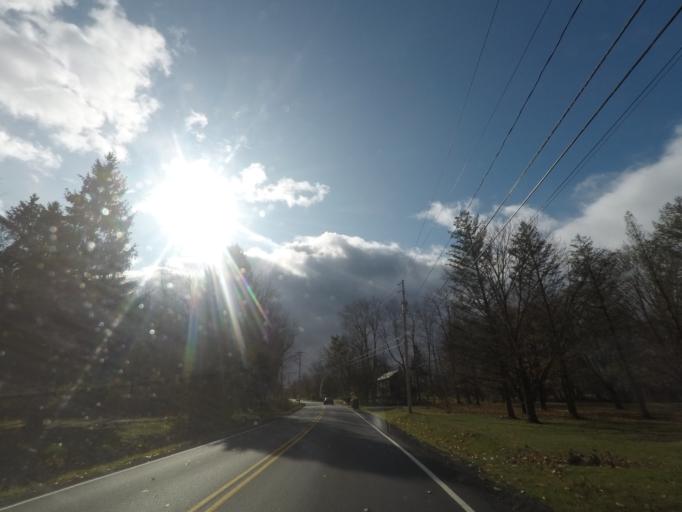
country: US
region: New York
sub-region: Saratoga County
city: Country Knolls
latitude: 42.9329
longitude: -73.8541
